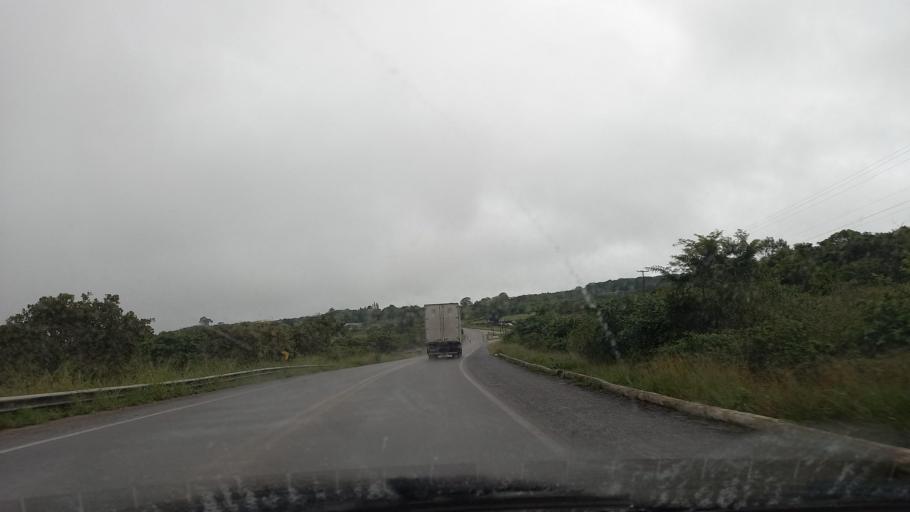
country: BR
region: Pernambuco
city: Garanhuns
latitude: -8.8743
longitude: -36.5323
